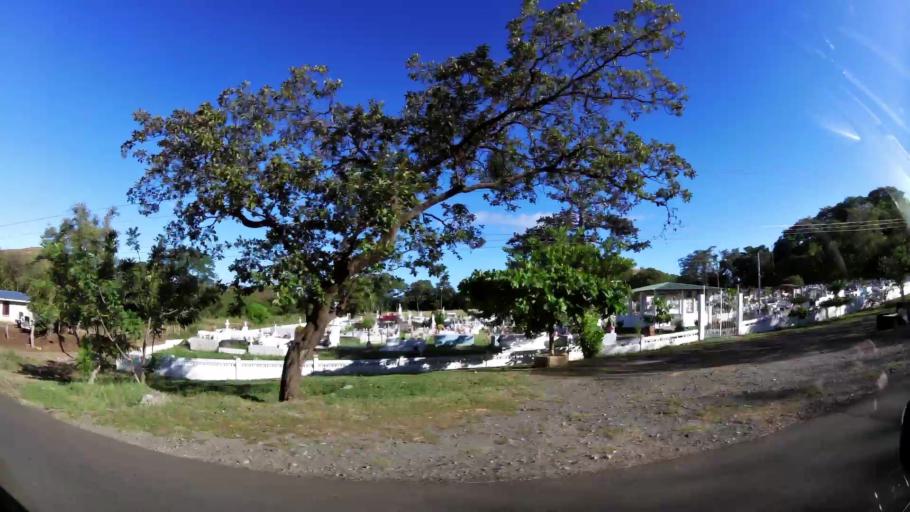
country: CR
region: Guanacaste
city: Sardinal
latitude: 10.4991
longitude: -85.6393
